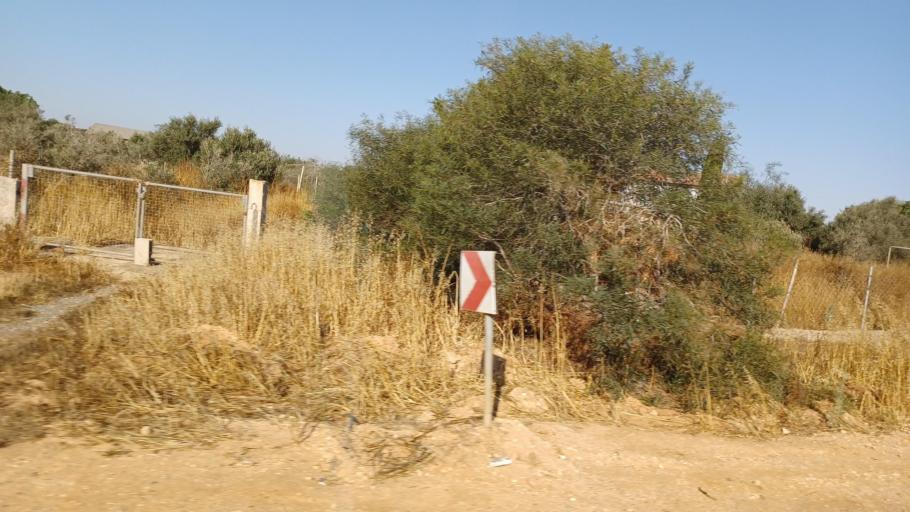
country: CY
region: Ammochostos
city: Frenaros
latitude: 35.0523
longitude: 33.9154
